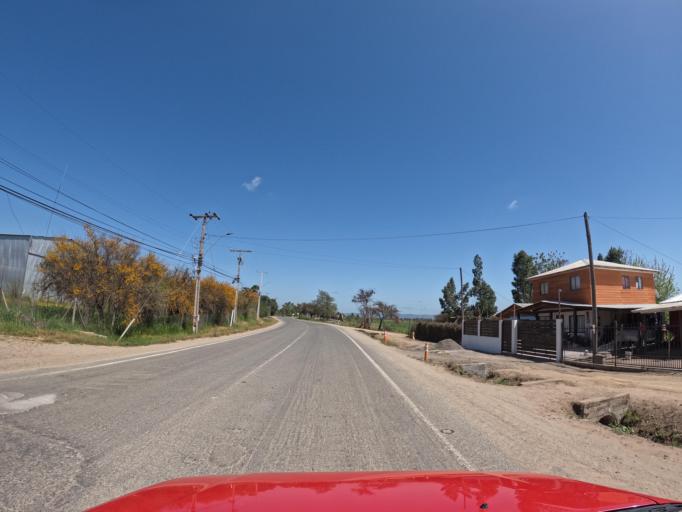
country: CL
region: O'Higgins
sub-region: Provincia de Colchagua
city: Santa Cruz
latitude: -34.7289
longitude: -71.6674
